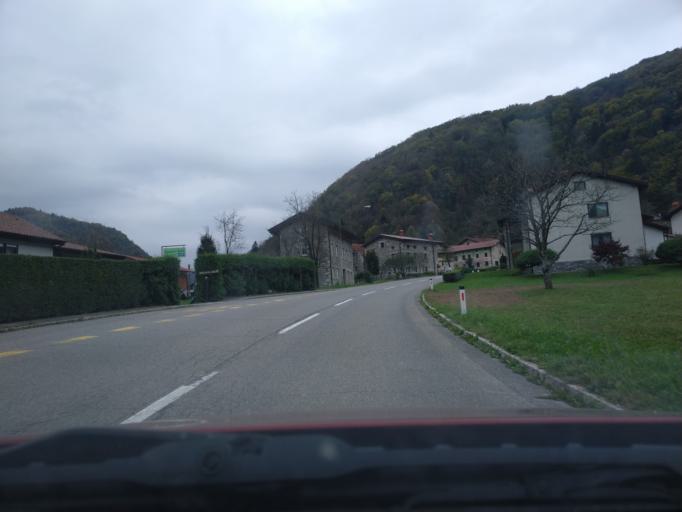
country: SI
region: Tolmin
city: Tolmin
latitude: 46.1644
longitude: 13.7101
